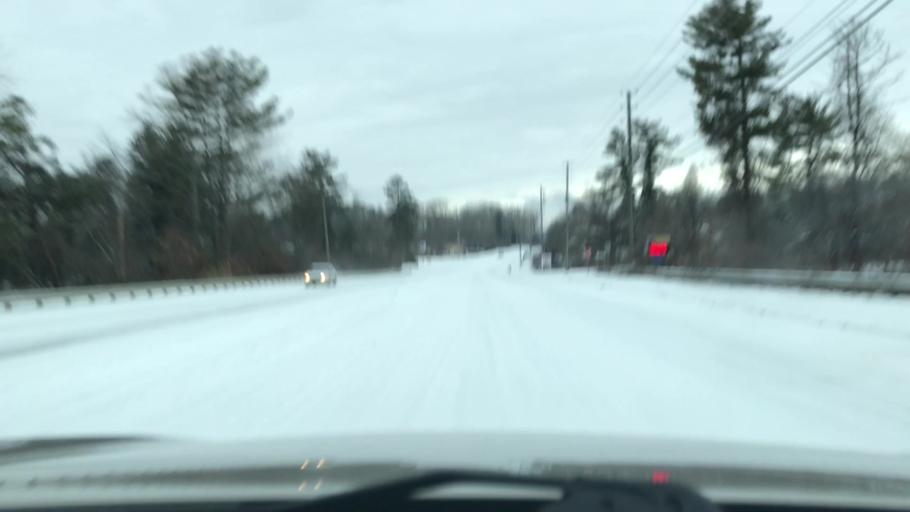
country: US
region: North Carolina
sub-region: Buncombe County
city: Royal Pines
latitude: 35.4837
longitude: -82.5331
